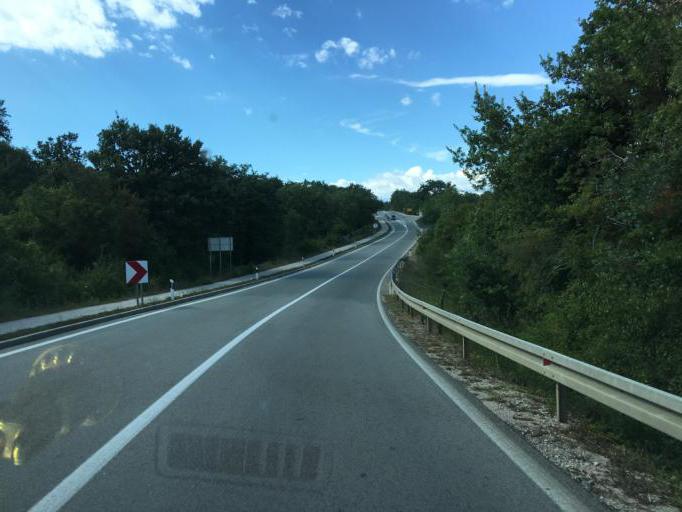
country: HR
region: Primorsko-Goranska
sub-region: Grad Krk
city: Krk
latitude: 45.0553
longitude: 14.5573
